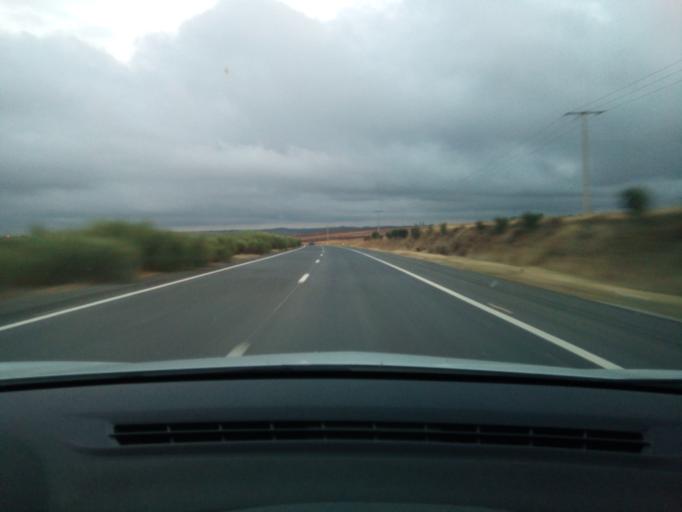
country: MA
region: Meknes-Tafilalet
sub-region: Meknes
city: Meknes
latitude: 33.8503
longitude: -5.6226
